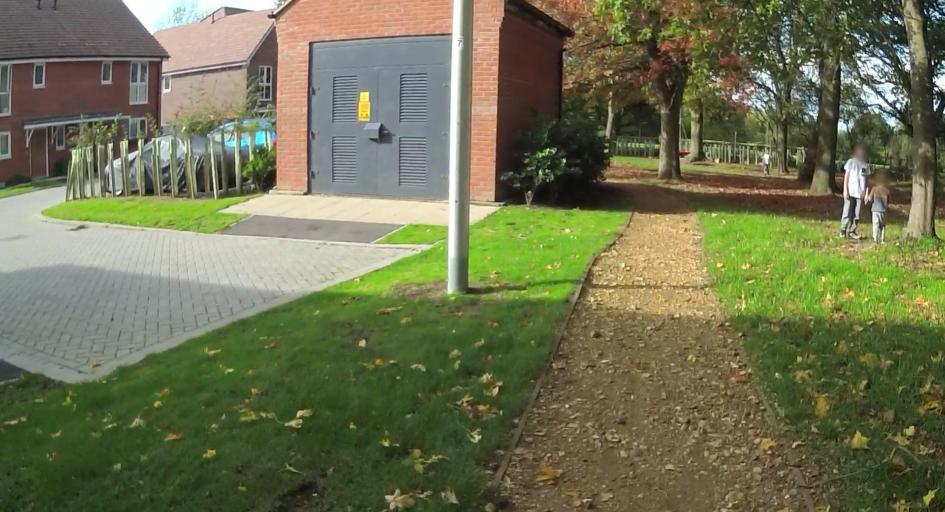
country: GB
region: England
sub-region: Wokingham
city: Barkham
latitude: 51.3876
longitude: -0.8854
